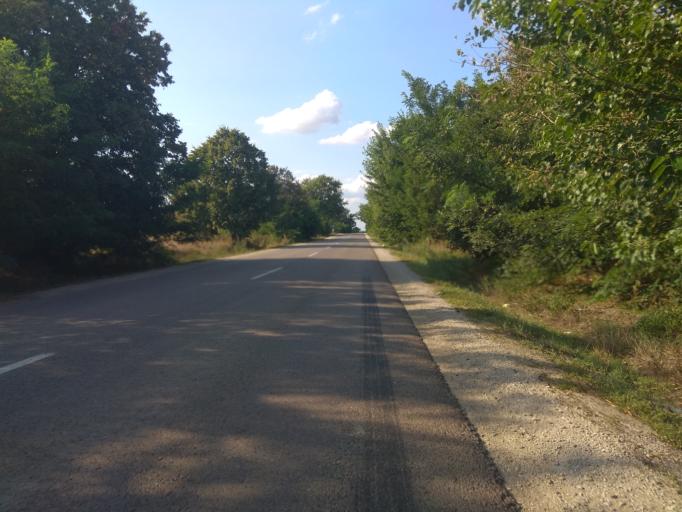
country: HU
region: Borsod-Abauj-Zemplen
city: Hejobaba
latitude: 47.8968
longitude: 20.8922
